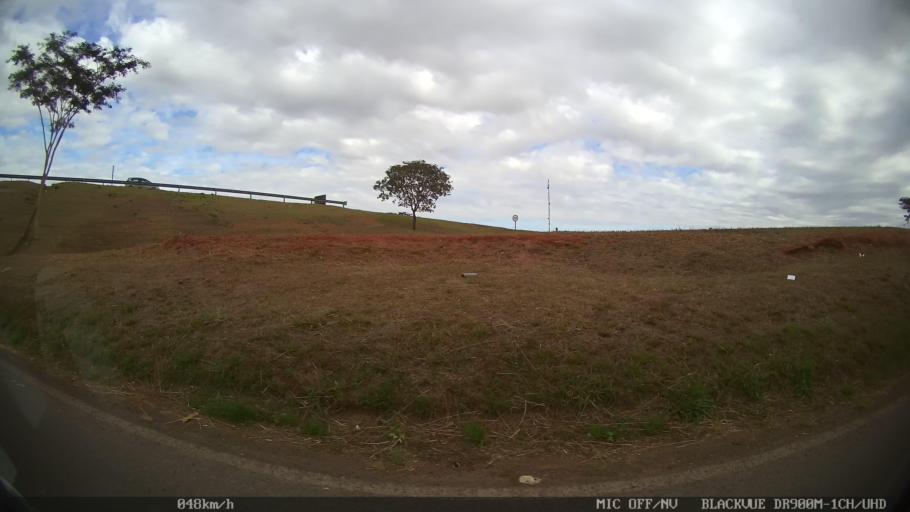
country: BR
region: Sao Paulo
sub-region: Bady Bassitt
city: Bady Bassitt
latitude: -20.8035
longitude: -49.5258
